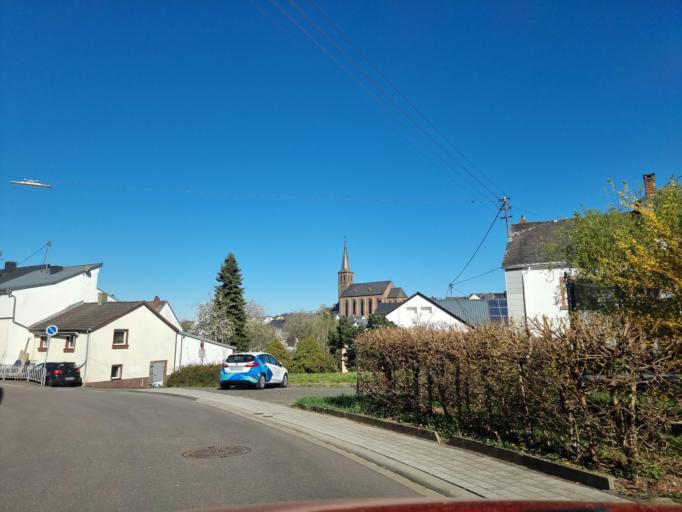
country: DE
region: Rheinland-Pfalz
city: Orenhofen
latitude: 49.8959
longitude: 6.6550
